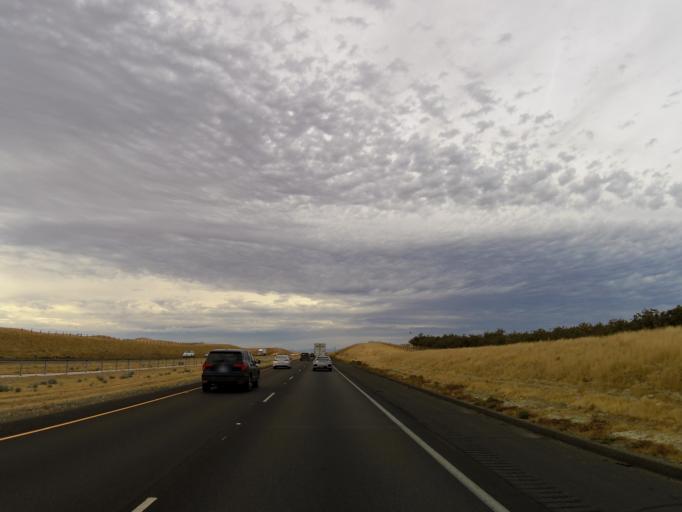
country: US
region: California
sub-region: Kings County
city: Kettleman City
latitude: 36.0389
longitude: -120.0375
